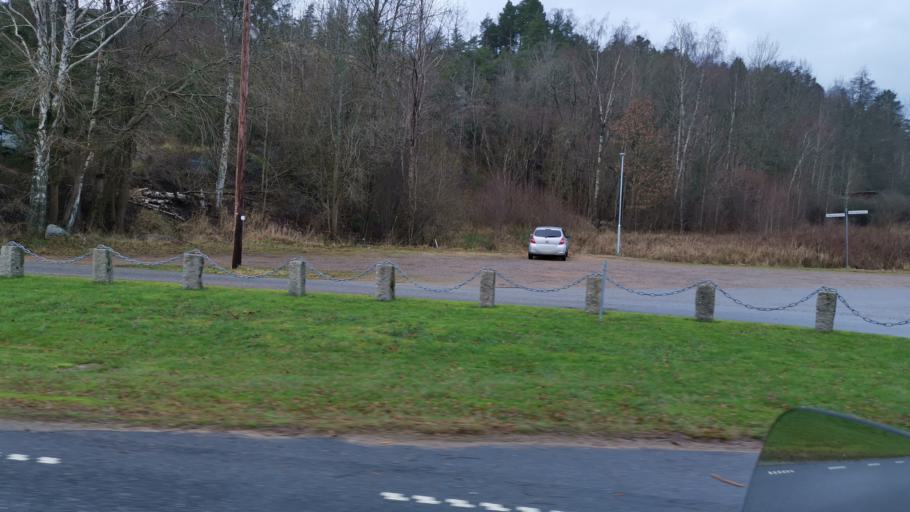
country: SE
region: Vaestra Goetaland
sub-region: Orust
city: Henan
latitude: 58.3387
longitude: 11.7274
